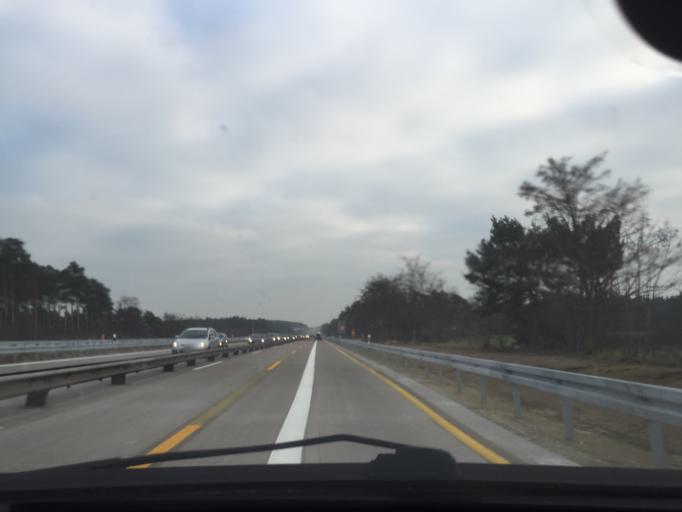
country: DE
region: Brandenburg
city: Golzow
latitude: 52.3452
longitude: 12.6216
